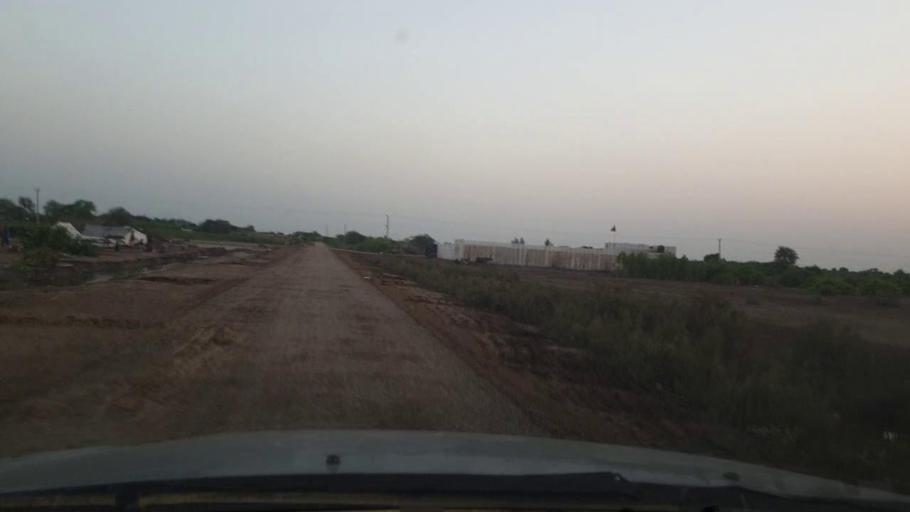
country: PK
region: Sindh
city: Digri
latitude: 25.1216
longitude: 69.0005
